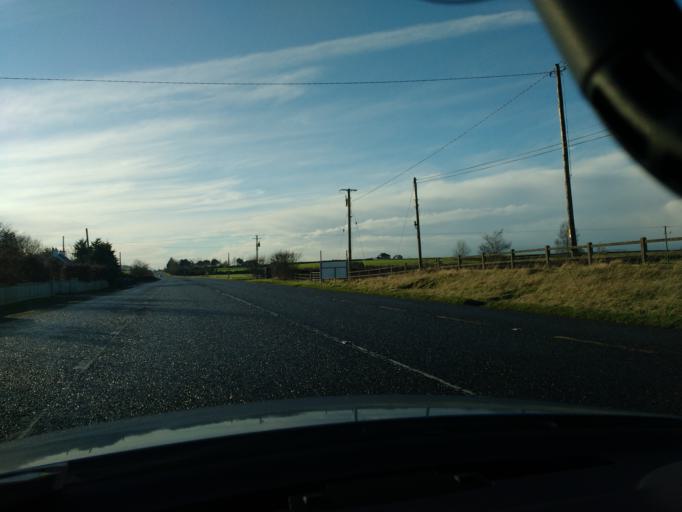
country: IE
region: Munster
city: Thurles
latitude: 52.6669
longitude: -7.6887
